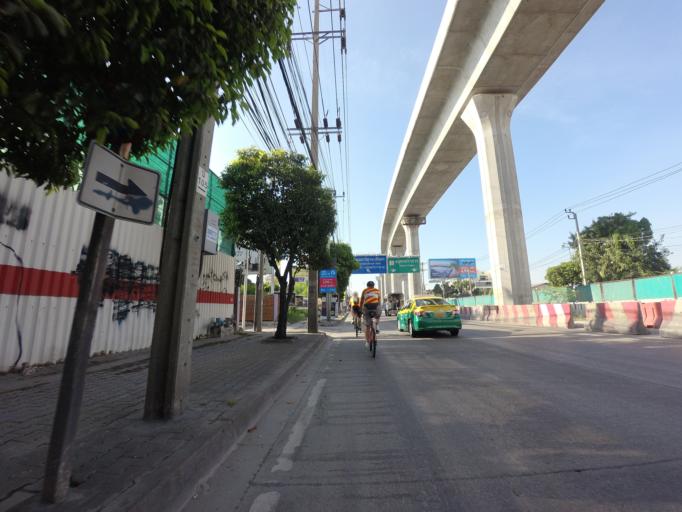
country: TH
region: Samut Prakan
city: Samut Prakan
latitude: 13.6342
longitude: 100.5909
